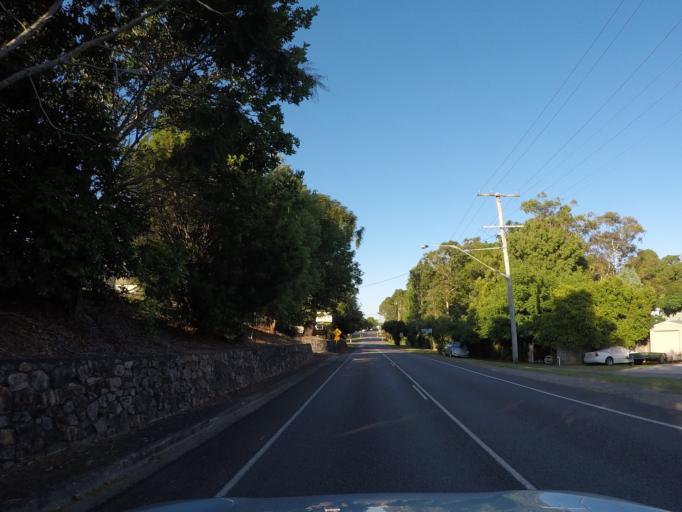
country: AU
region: Queensland
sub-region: Sunshine Coast
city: Nambour
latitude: -26.6261
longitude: 152.8634
